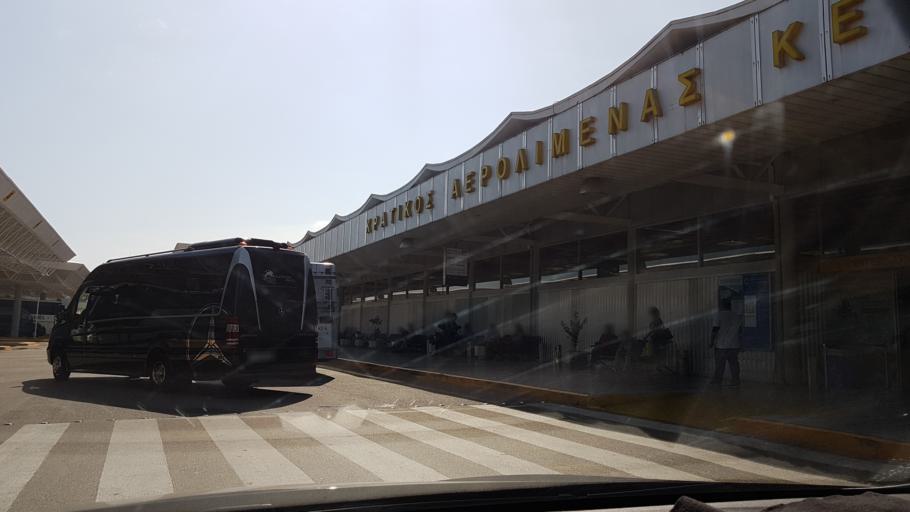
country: GR
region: Ionian Islands
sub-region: Nomos Kerkyras
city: Kerkyra
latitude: 39.6078
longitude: 19.9148
